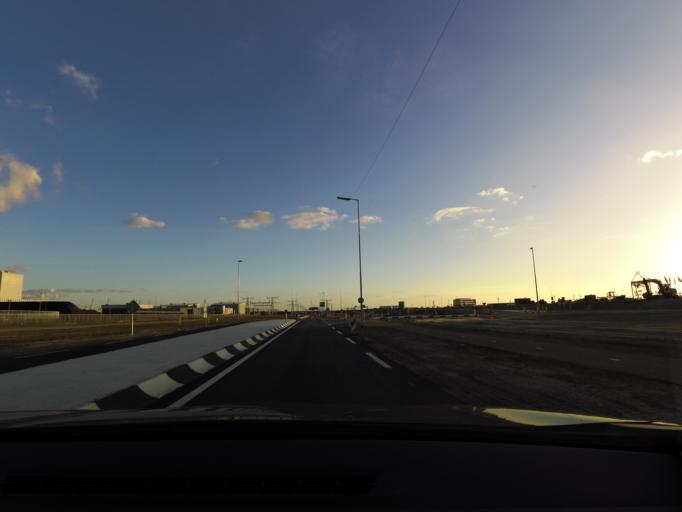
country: NL
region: South Holland
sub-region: Gemeente Rotterdam
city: Hoek van Holland
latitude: 51.9614
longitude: 4.0163
